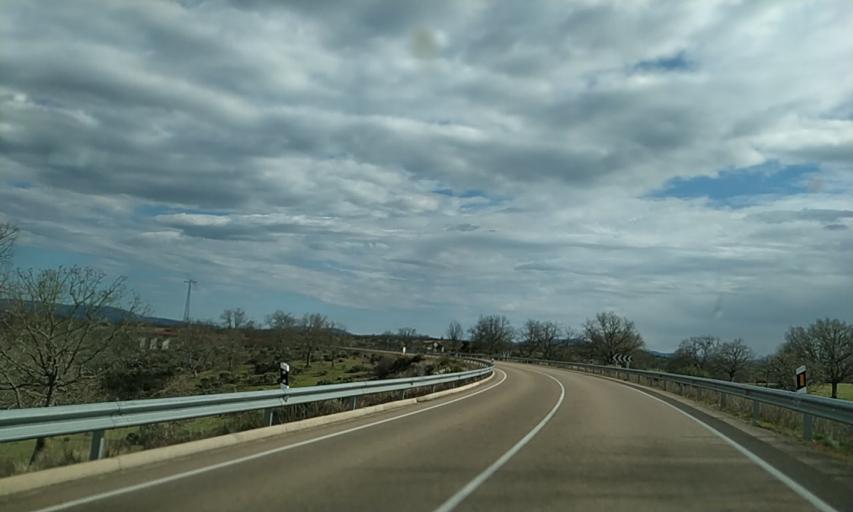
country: ES
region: Castille and Leon
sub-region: Provincia de Salamanca
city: Robleda
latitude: 40.4328
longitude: -6.6052
